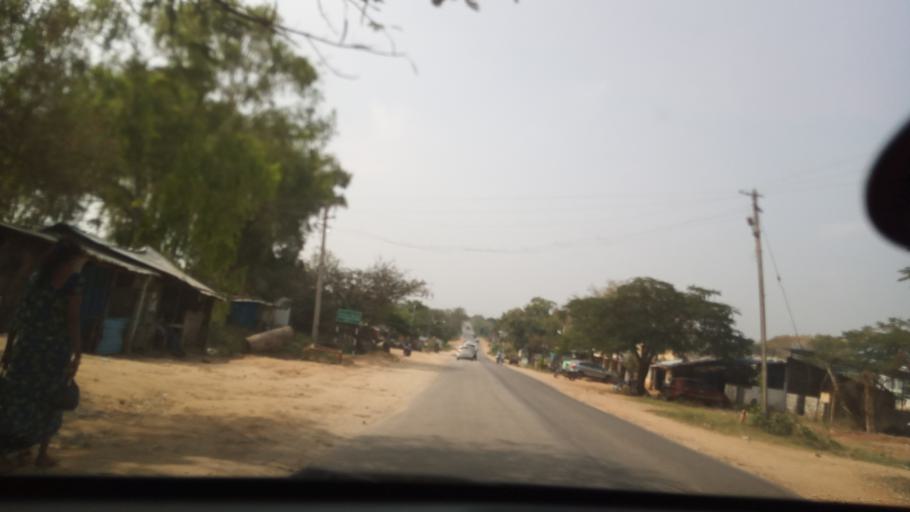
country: IN
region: Karnataka
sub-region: Chamrajnagar
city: Chamrajnagar
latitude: 11.9934
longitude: 76.8598
